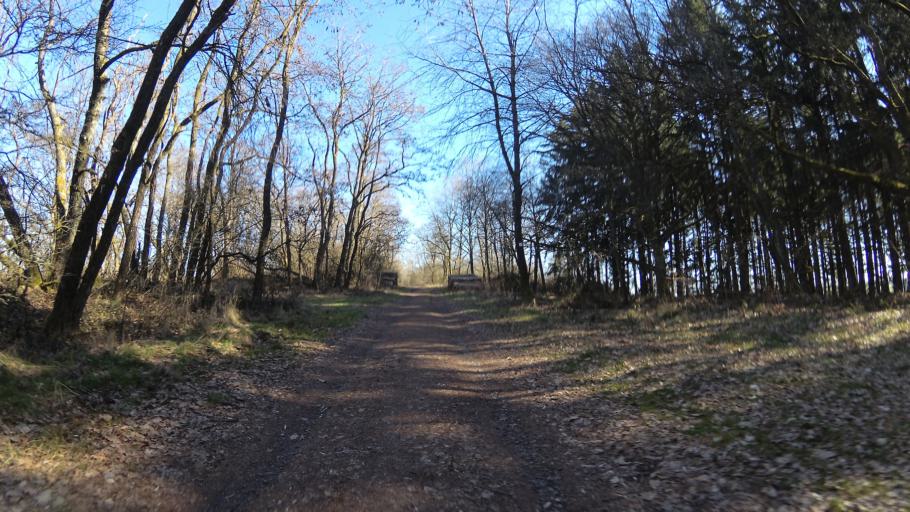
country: DE
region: Rheinland-Pfalz
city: Breitenbach
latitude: 49.4568
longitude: 7.2601
